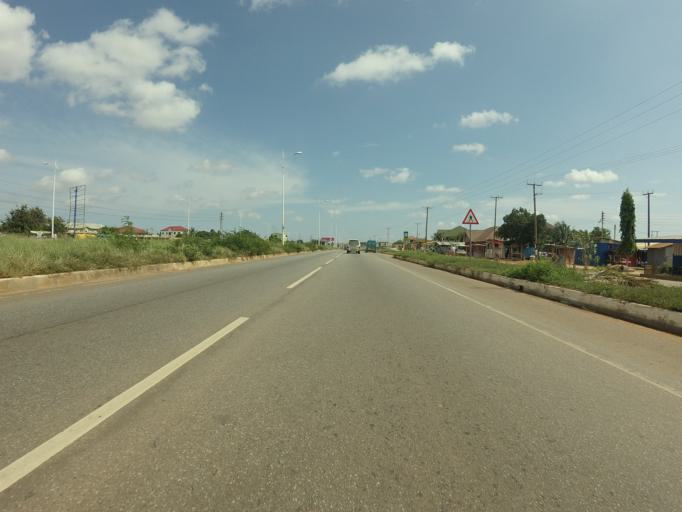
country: GH
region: Greater Accra
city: Medina Estates
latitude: 5.7145
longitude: -0.1720
